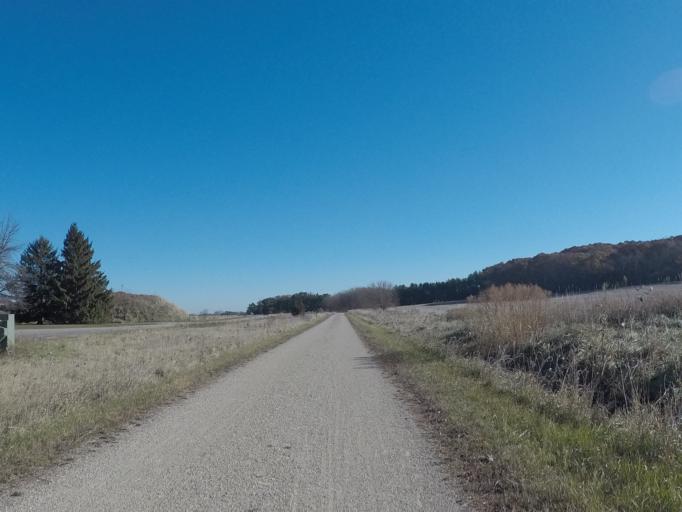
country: US
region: Wisconsin
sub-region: Jefferson County
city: Lake Mills
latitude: 43.0650
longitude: -88.9605
